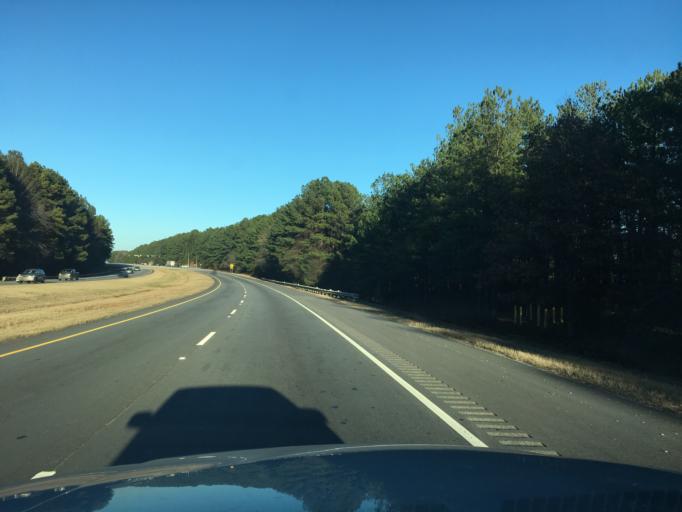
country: US
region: Georgia
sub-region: Carroll County
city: Carrollton
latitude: 33.5589
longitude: -85.0608
